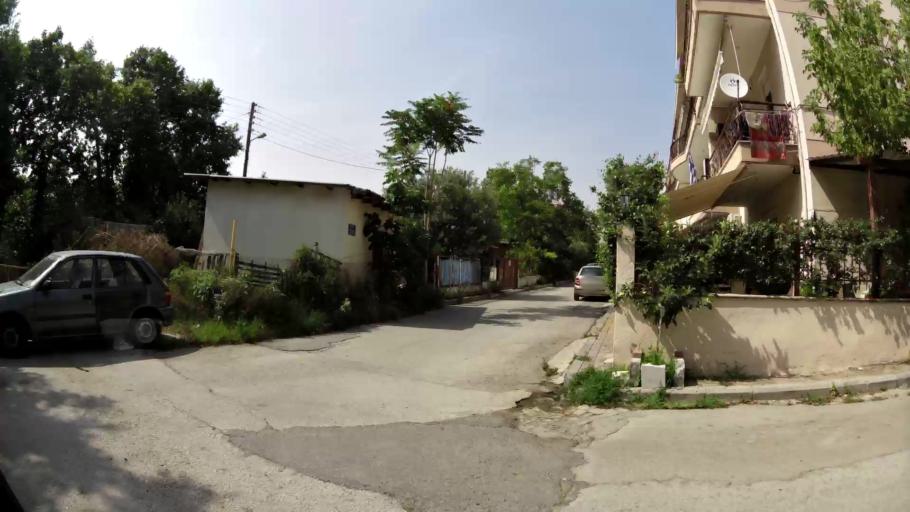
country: GR
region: Central Macedonia
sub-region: Nomos Thessalonikis
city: Efkarpia
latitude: 40.6827
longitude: 22.9433
